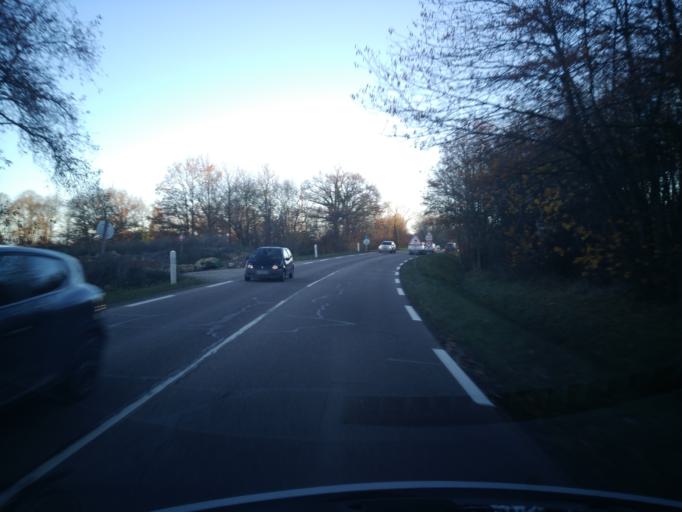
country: FR
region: Ile-de-France
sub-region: Departement des Yvelines
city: Orgeval
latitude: 48.8988
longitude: 2.0014
